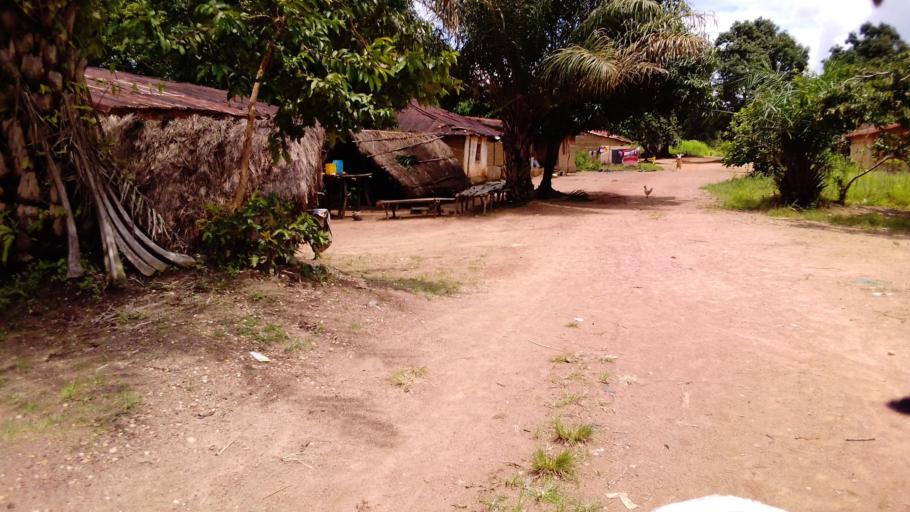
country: SL
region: Eastern Province
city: Koidu
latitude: 8.6777
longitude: -10.9568
